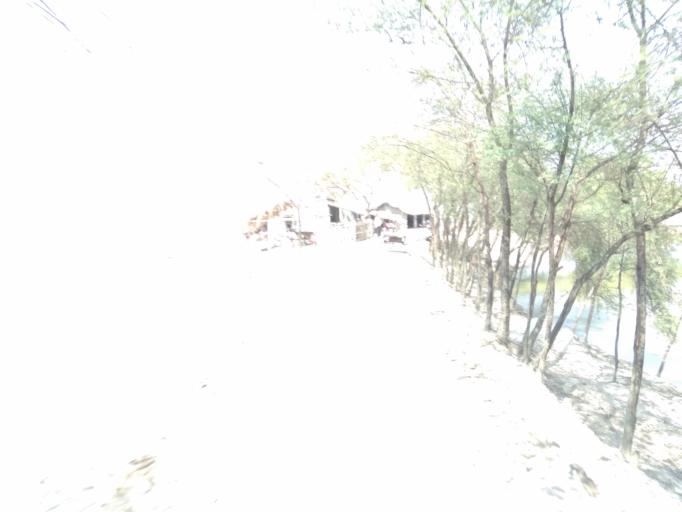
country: IN
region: West Bengal
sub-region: North 24 Parganas
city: Taki
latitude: 22.3954
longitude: 89.1915
